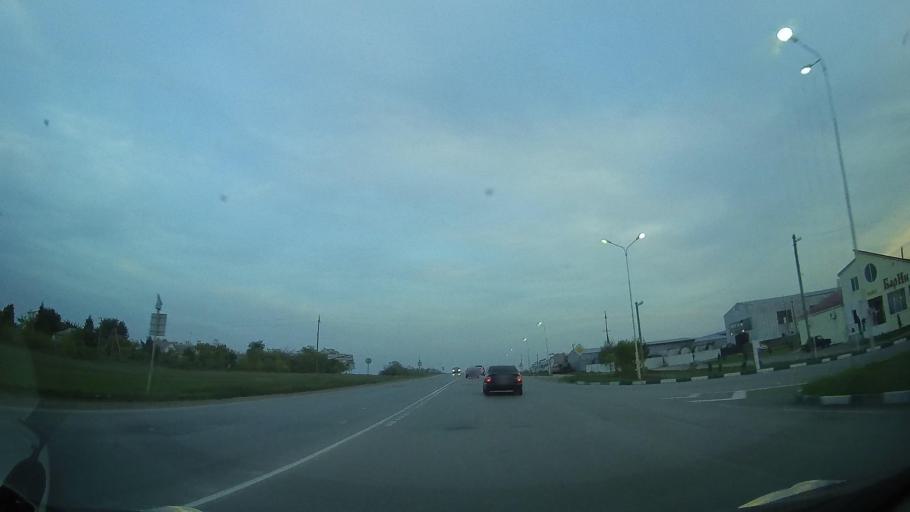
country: RU
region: Rostov
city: Kagal'nitskaya
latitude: 46.8763
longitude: 40.1584
